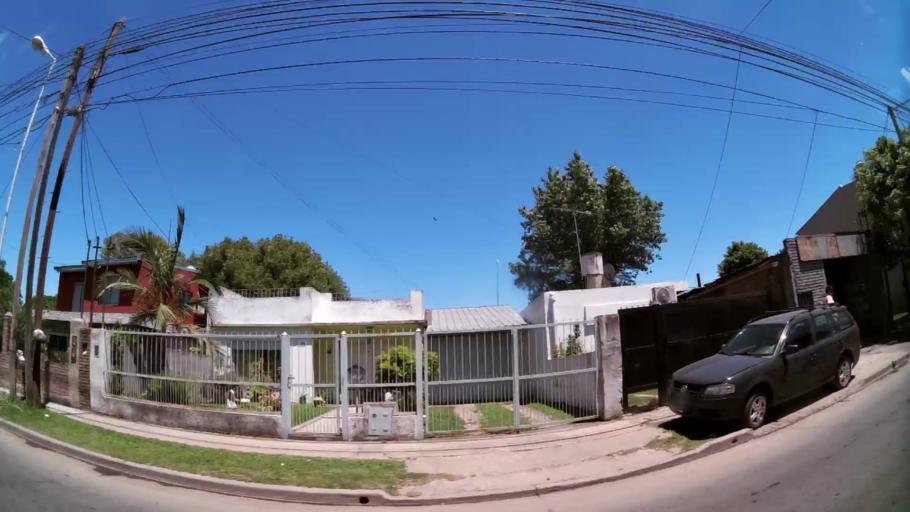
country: AR
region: Buenos Aires
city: Hurlingham
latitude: -34.5054
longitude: -58.7160
